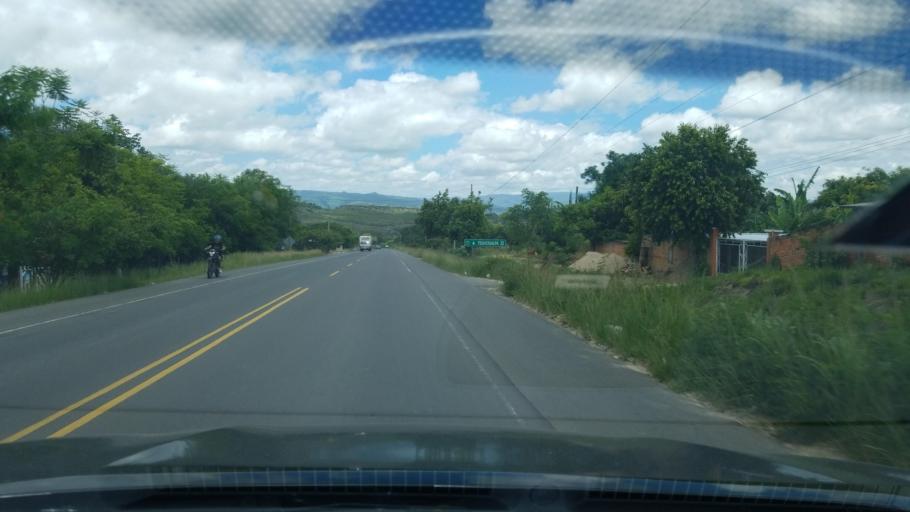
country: HN
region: Francisco Morazan
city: Cofradia
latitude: 14.3148
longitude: -87.2141
